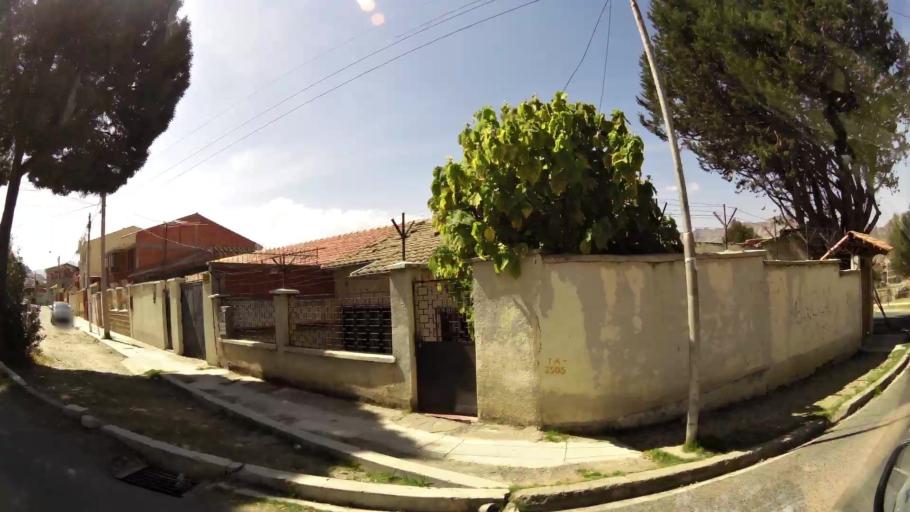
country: BO
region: La Paz
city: La Paz
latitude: -16.5382
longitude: -68.1013
